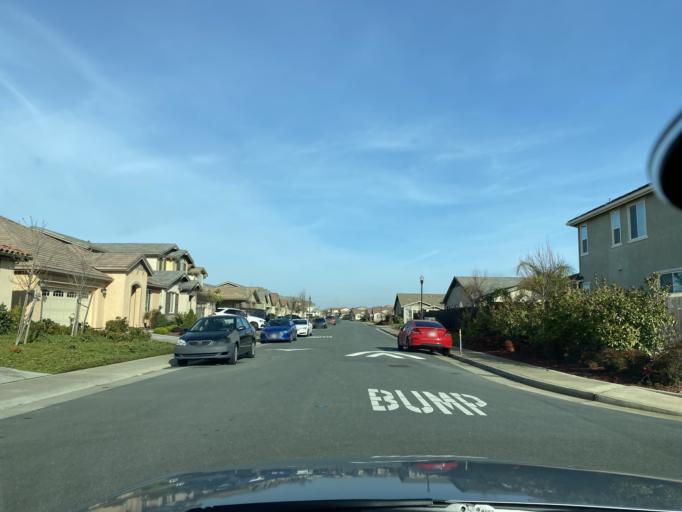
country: US
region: California
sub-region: Sacramento County
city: Elk Grove
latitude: 38.3958
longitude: -121.3859
